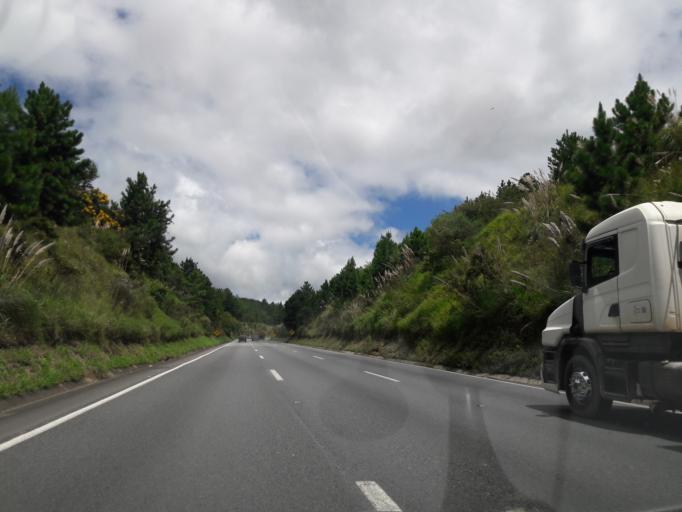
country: BR
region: Parana
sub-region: Campina Grande Do Sul
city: Campina Grande do Sul
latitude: -25.1032
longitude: -48.8349
